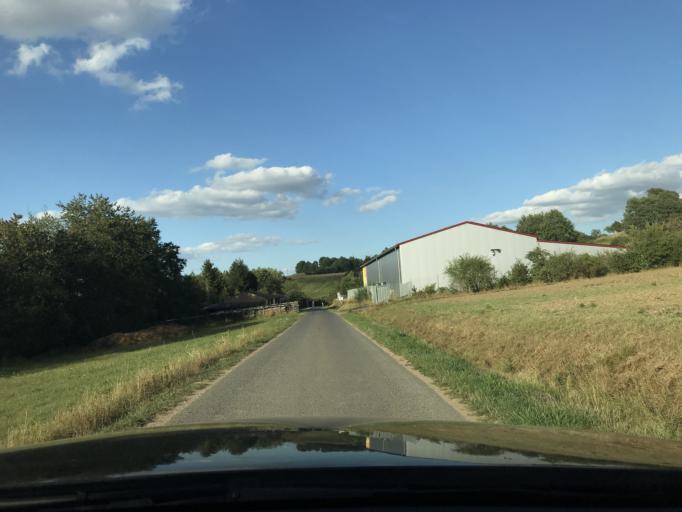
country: DE
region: Bavaria
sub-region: Regierungsbezirk Unterfranken
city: Breitbrunn
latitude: 50.0291
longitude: 10.6850
